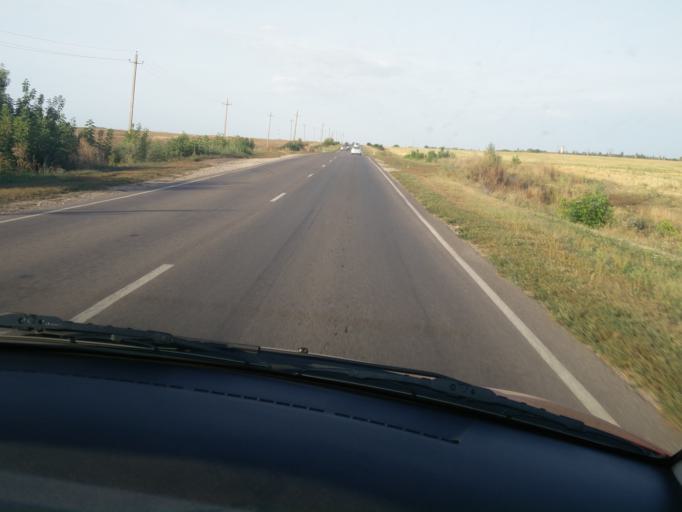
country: RU
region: Voronezj
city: Ramon'
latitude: 51.9276
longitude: 39.3267
